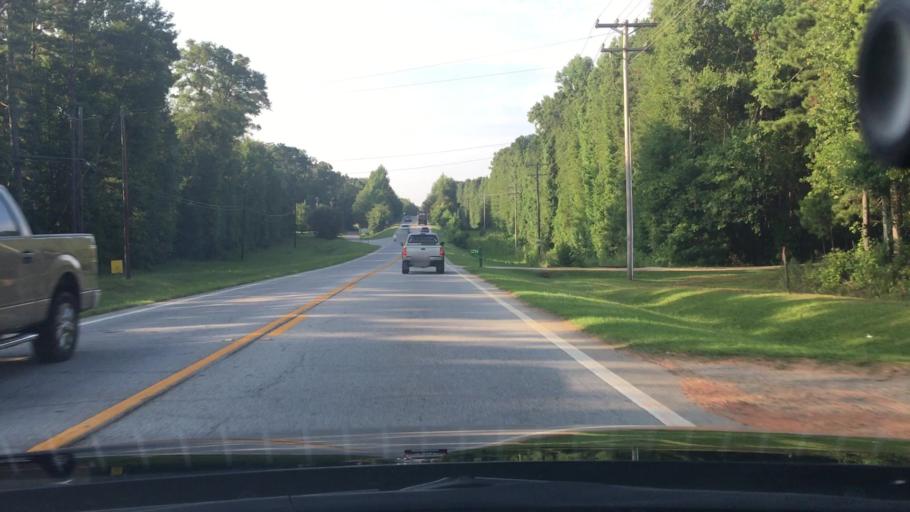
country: US
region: Georgia
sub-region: Fayette County
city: Peachtree City
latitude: 33.3345
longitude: -84.6469
